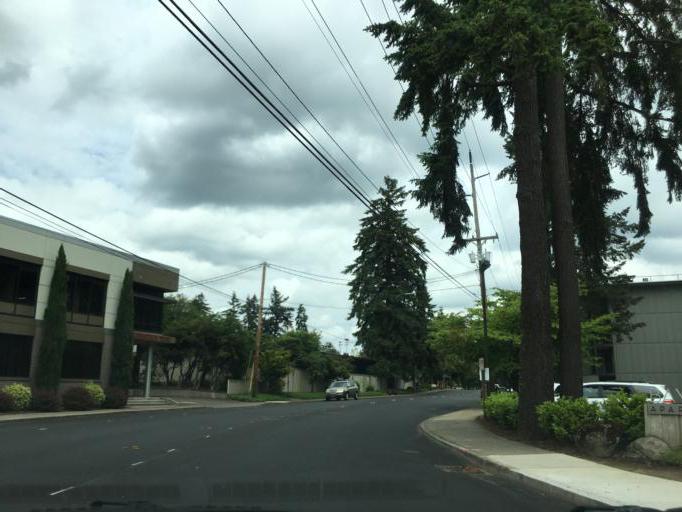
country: US
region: Oregon
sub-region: Clackamas County
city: Lake Oswego
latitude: 45.4105
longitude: -122.6672
